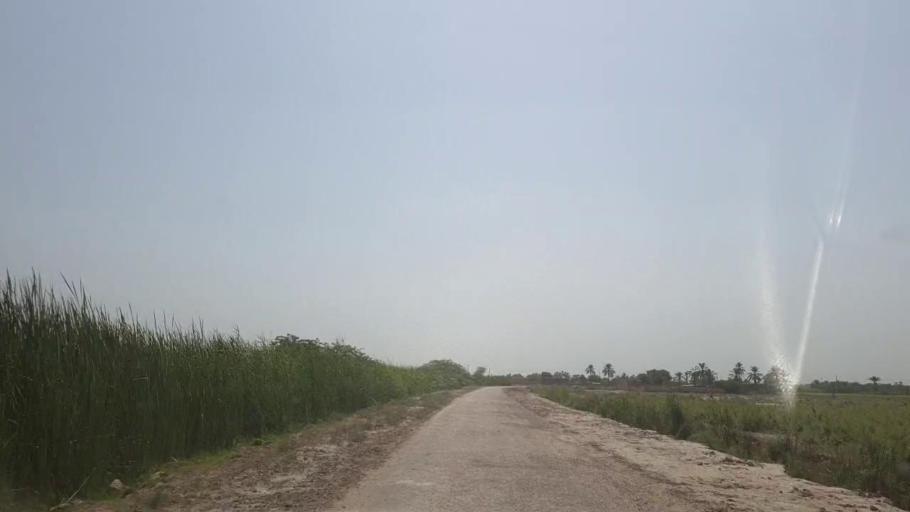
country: PK
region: Sindh
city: Gambat
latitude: 27.3129
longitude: 68.5434
